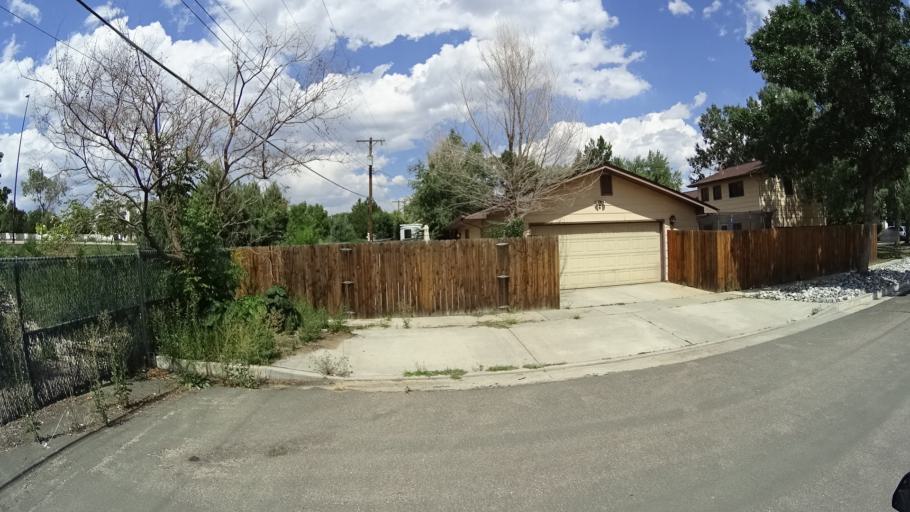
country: US
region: Colorado
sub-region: El Paso County
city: Colorado Springs
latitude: 38.8273
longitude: -104.7805
